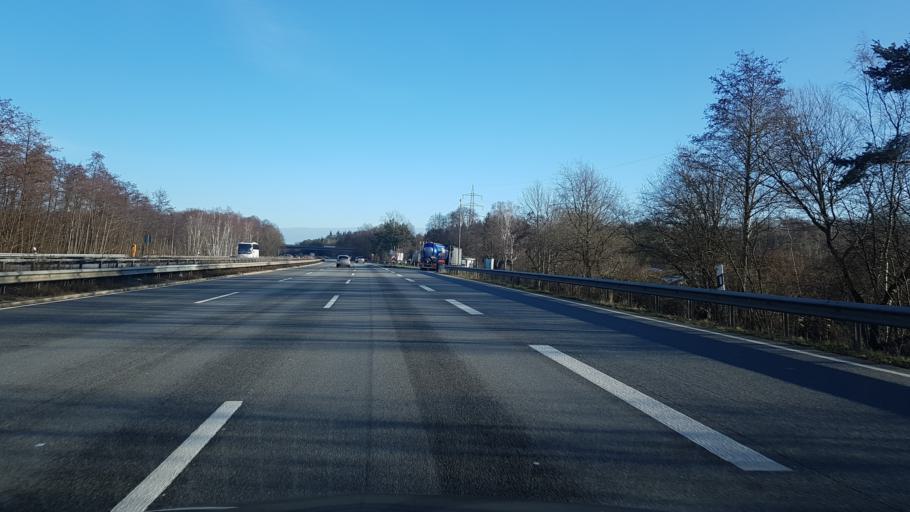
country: DE
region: Rheinland-Pfalz
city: Kindsbach
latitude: 49.4230
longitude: 7.6088
